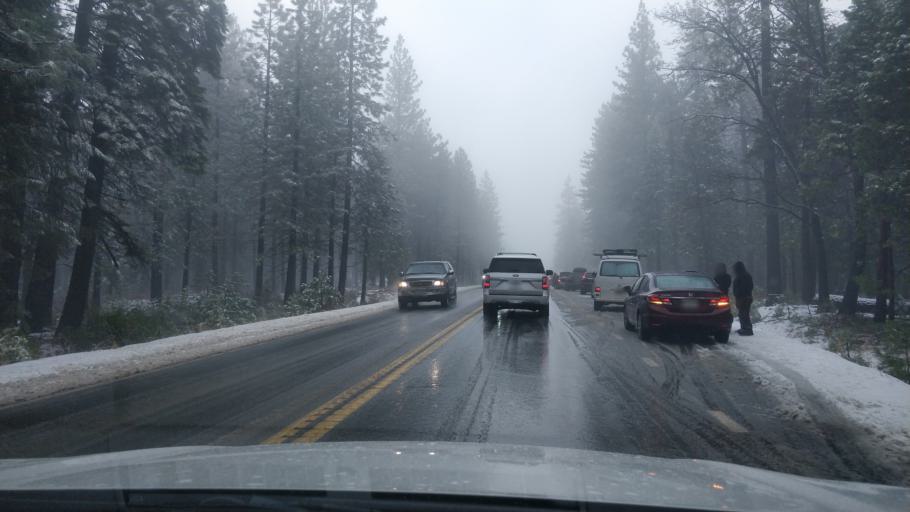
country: US
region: California
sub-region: Sierra County
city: Downieville
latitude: 39.3126
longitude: -120.7552
